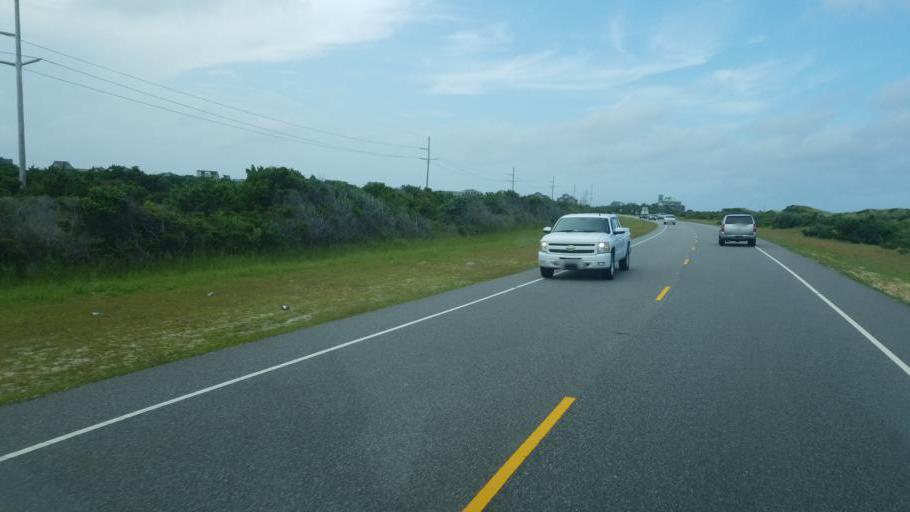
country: US
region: North Carolina
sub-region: Dare County
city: Buxton
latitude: 35.3178
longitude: -75.5098
